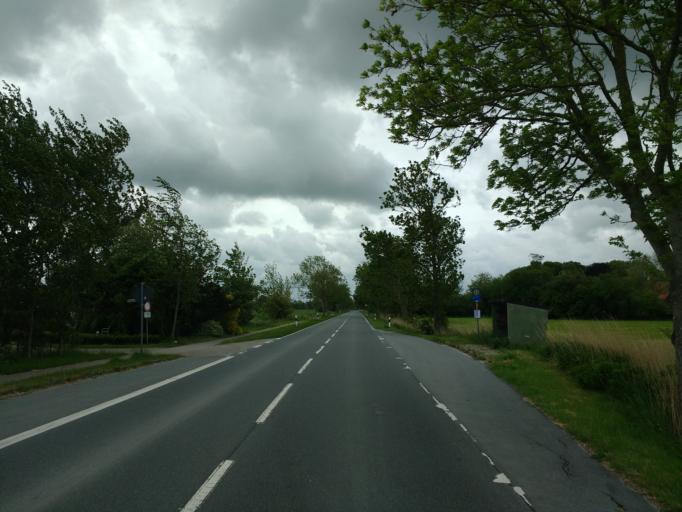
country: DE
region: Lower Saxony
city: Schillig
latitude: 53.6782
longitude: 7.9883
